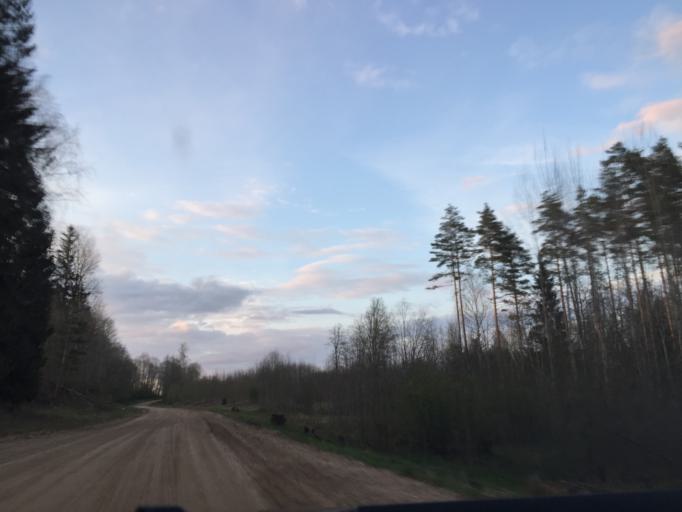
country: LV
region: Aluksnes Rajons
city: Aluksne
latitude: 57.3106
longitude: 26.9148
